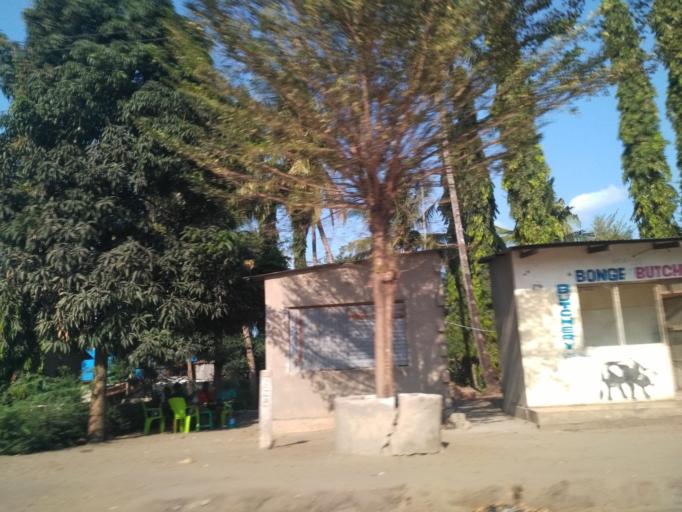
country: TZ
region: Dar es Salaam
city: Dar es Salaam
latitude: -6.8542
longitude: 39.3179
